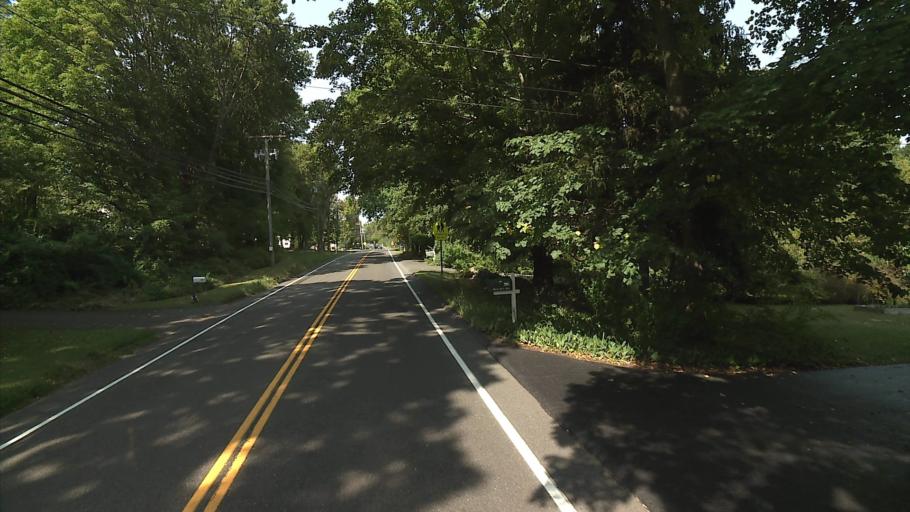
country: US
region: Connecticut
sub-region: Fairfield County
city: Bethel
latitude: 41.3126
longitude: -73.3497
